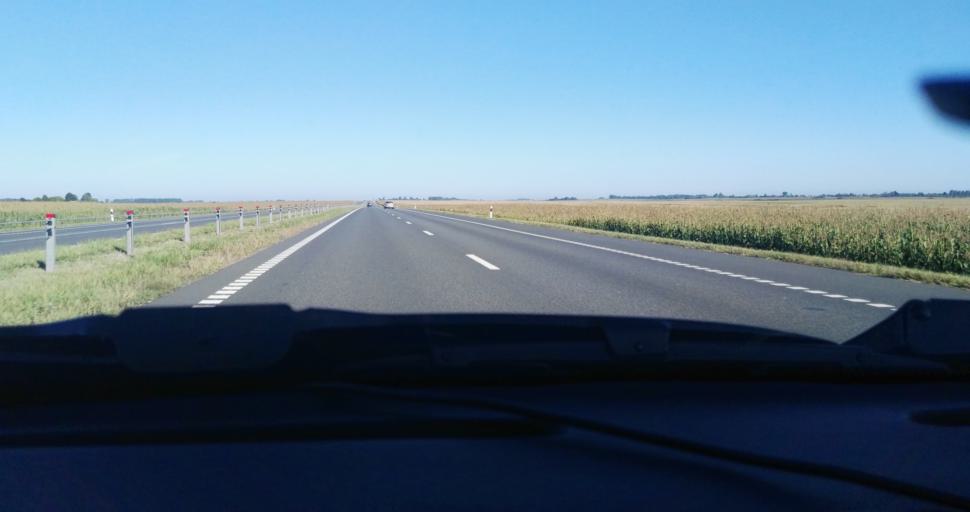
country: BY
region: Gomel
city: Buda-Kashalyova
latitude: 52.5254
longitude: 30.6171
